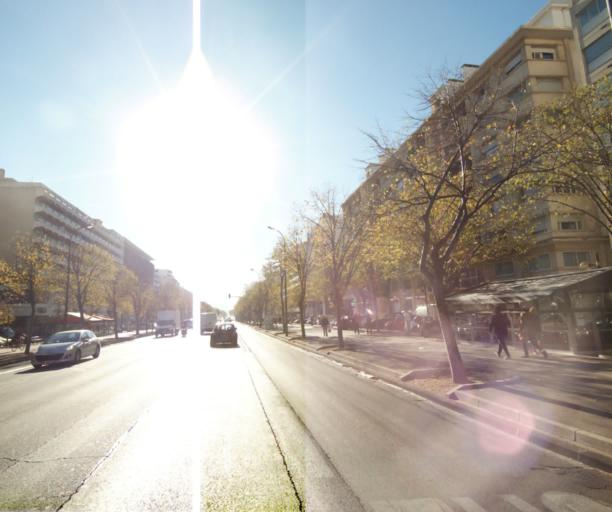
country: FR
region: Provence-Alpes-Cote d'Azur
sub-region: Departement des Bouches-du-Rhone
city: Marseille 08
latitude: 43.2759
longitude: 5.3893
